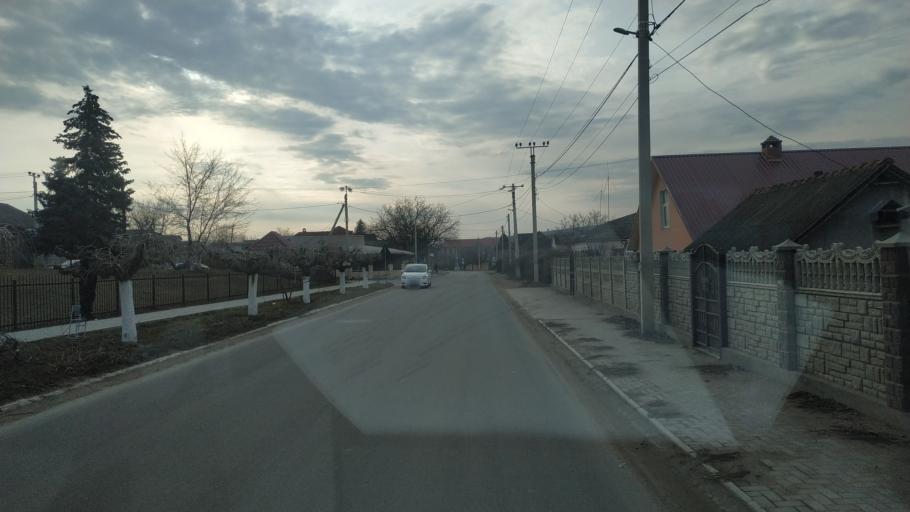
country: MD
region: Chisinau
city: Singera
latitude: 46.9649
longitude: 29.0543
